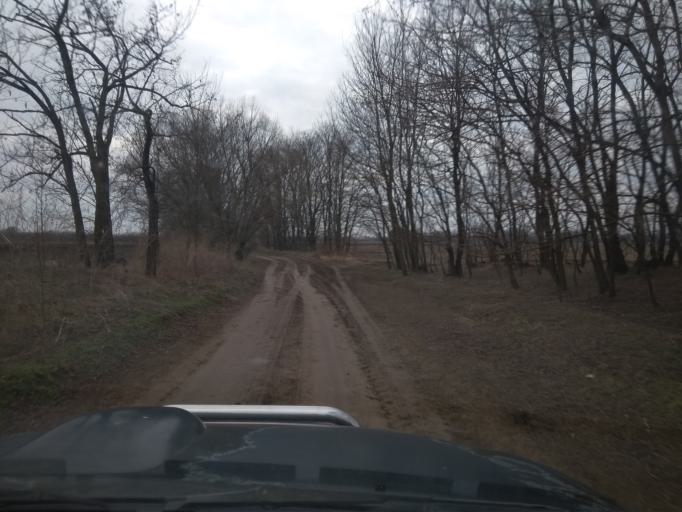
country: HU
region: Szabolcs-Szatmar-Bereg
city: Nyirtelek
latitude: 47.9680
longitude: 21.6551
